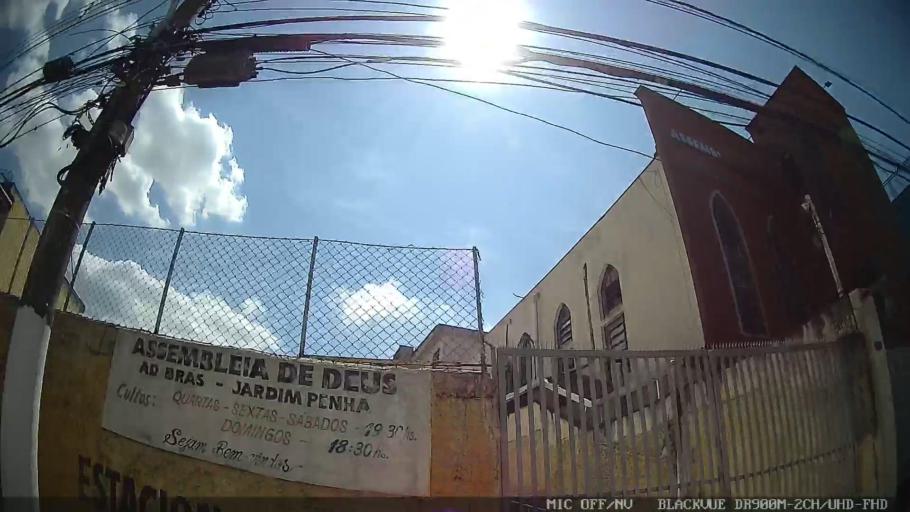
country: BR
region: Sao Paulo
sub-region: Guarulhos
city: Guarulhos
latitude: -23.5042
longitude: -46.4939
